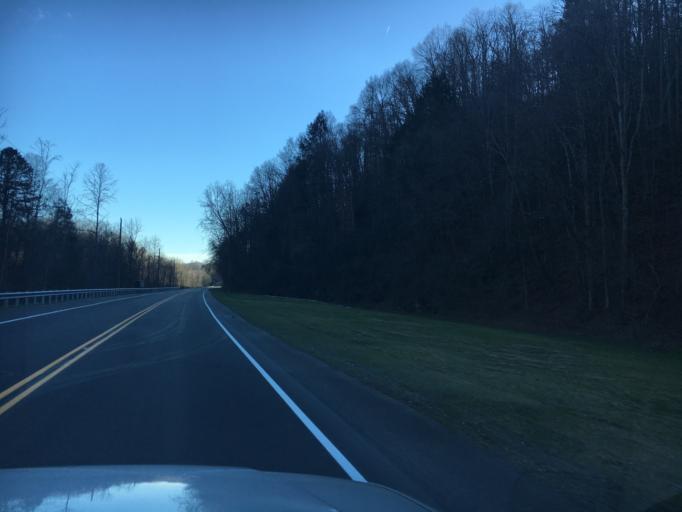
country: US
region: North Carolina
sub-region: McDowell County
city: West Marion
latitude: 35.5723
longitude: -81.9741
